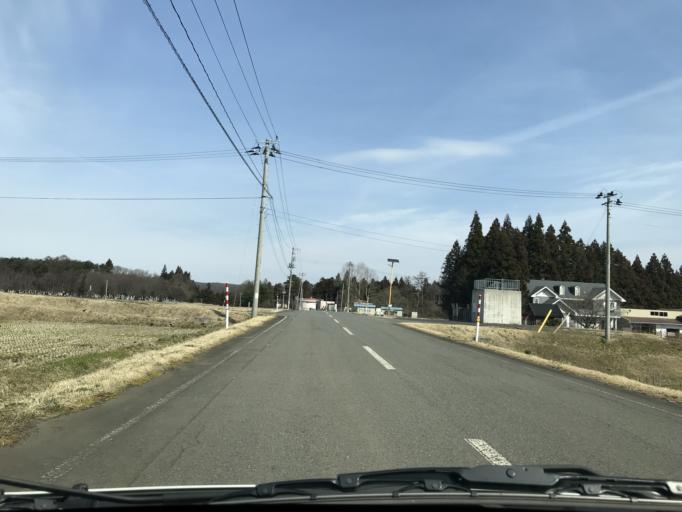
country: JP
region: Iwate
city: Mizusawa
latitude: 39.1153
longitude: 141.0127
